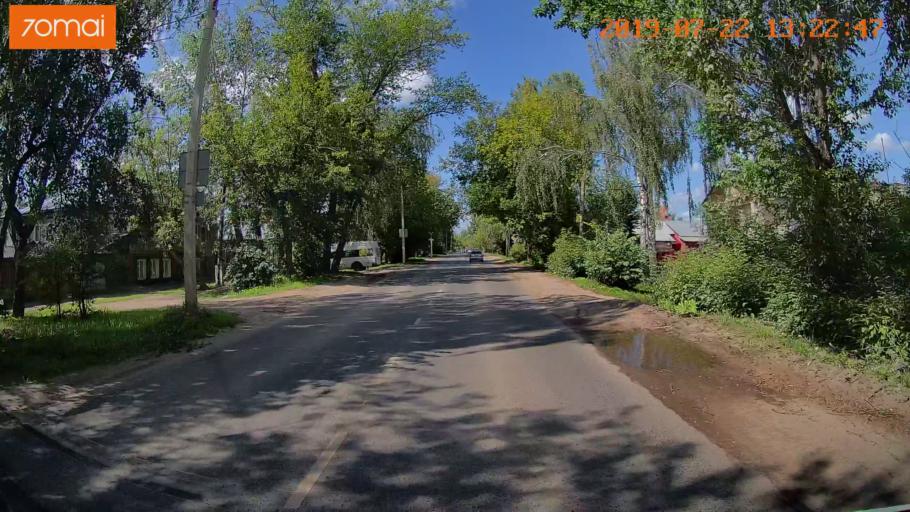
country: RU
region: Ivanovo
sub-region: Gorod Ivanovo
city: Ivanovo
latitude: 57.0249
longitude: 40.9544
